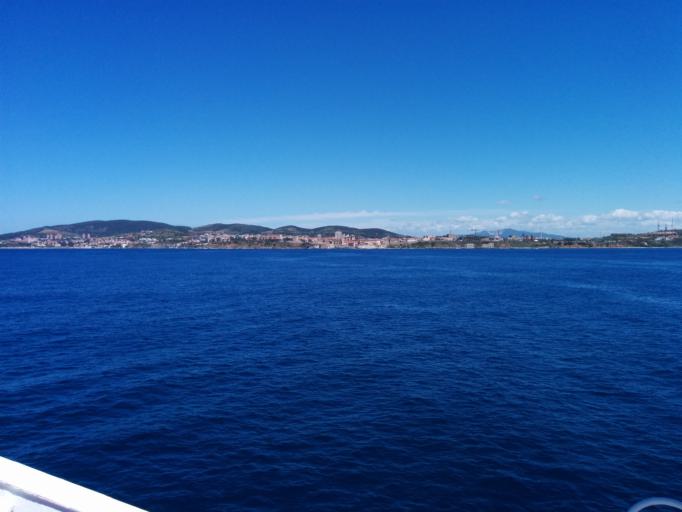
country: IT
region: Tuscany
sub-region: Provincia di Livorno
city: Piombino
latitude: 42.9027
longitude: 10.5221
